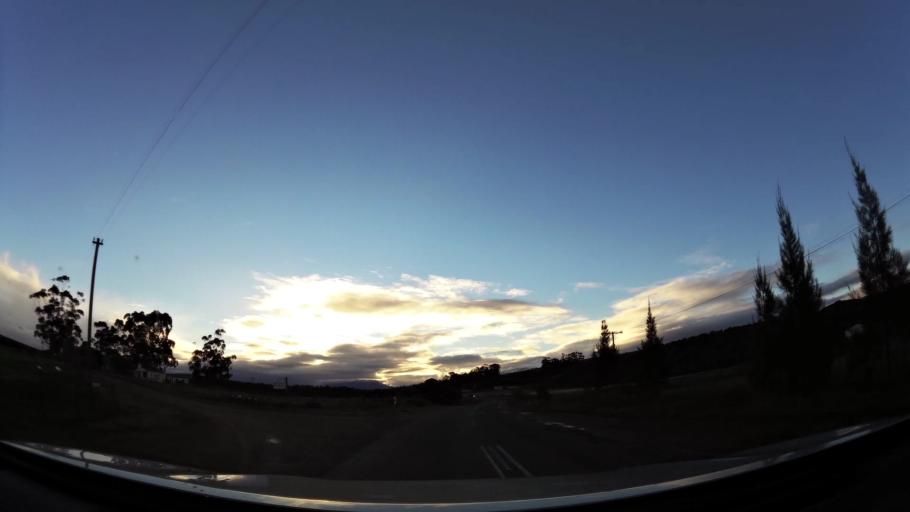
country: ZA
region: Western Cape
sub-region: Eden District Municipality
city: Riversdale
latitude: -34.0783
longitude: 20.9231
